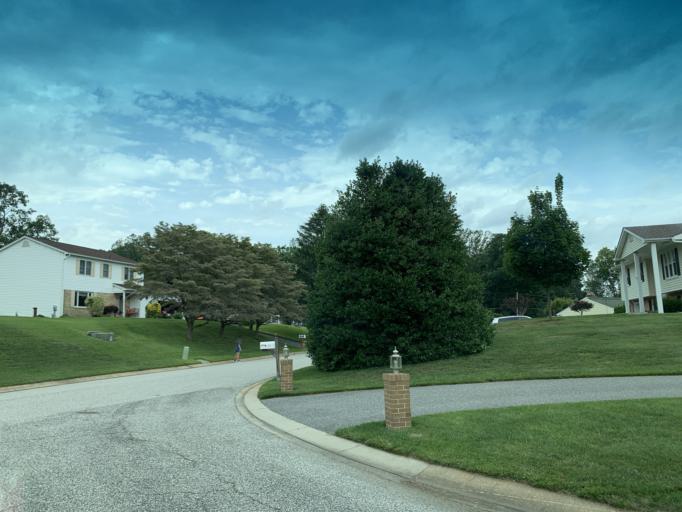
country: US
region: Maryland
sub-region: Harford County
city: Fallston
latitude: 39.5357
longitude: -76.4348
